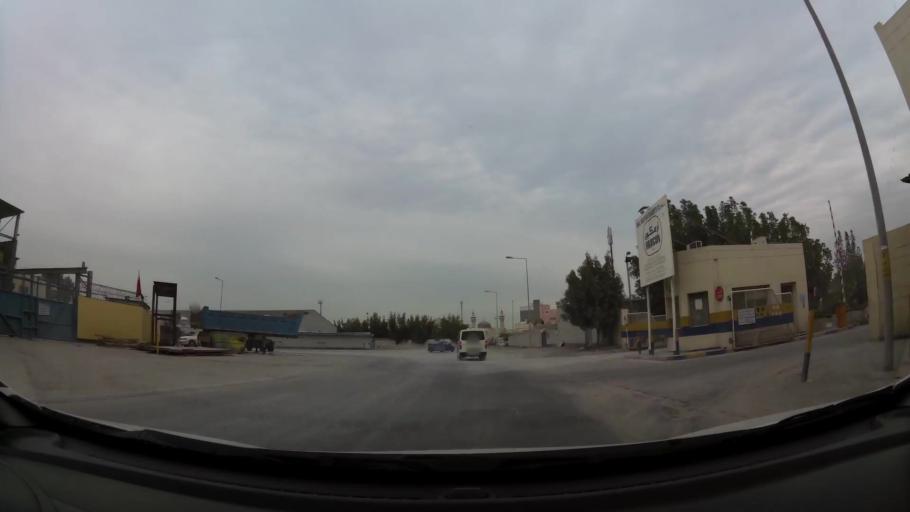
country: BH
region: Northern
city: Sitrah
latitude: 26.1316
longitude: 50.6115
